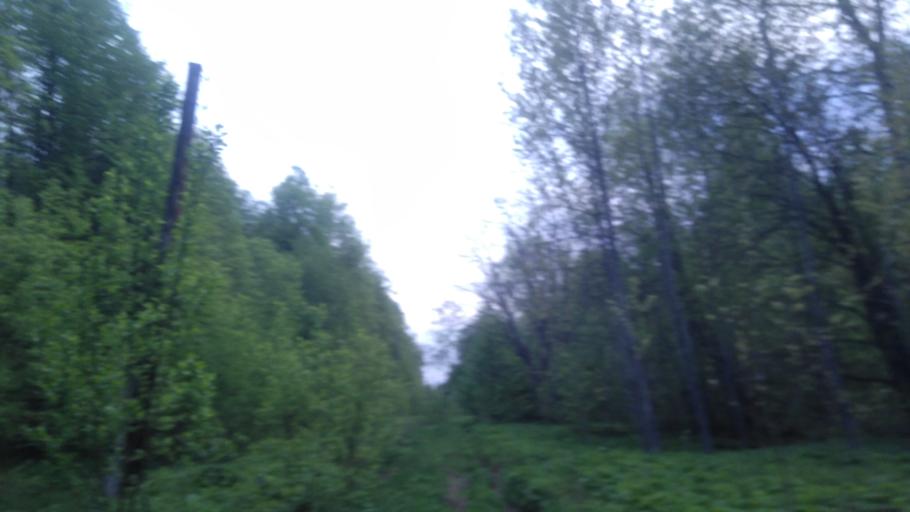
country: RU
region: Perm
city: Froly
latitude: 57.9653
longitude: 56.2908
